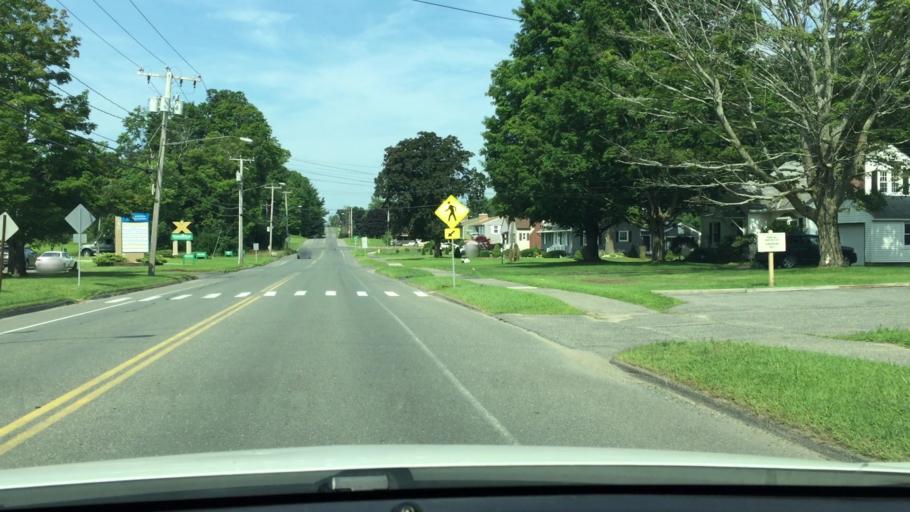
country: US
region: Massachusetts
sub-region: Berkshire County
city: Pittsfield
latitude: 42.4323
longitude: -73.2133
